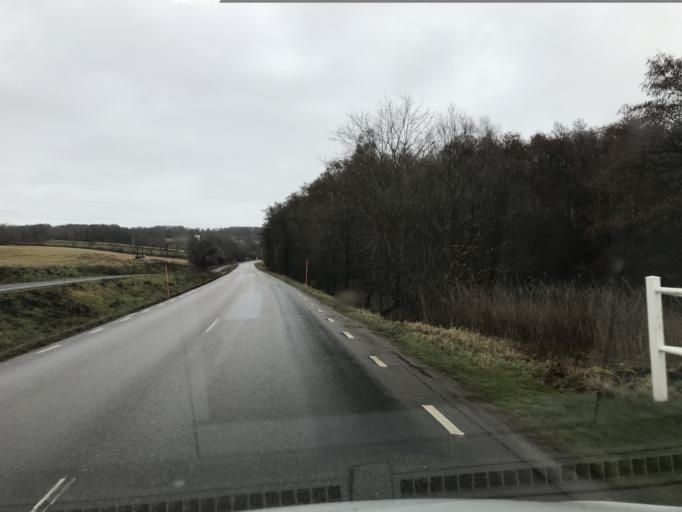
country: SE
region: Skane
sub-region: Bastads Kommun
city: Forslov
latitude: 56.3526
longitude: 12.8346
